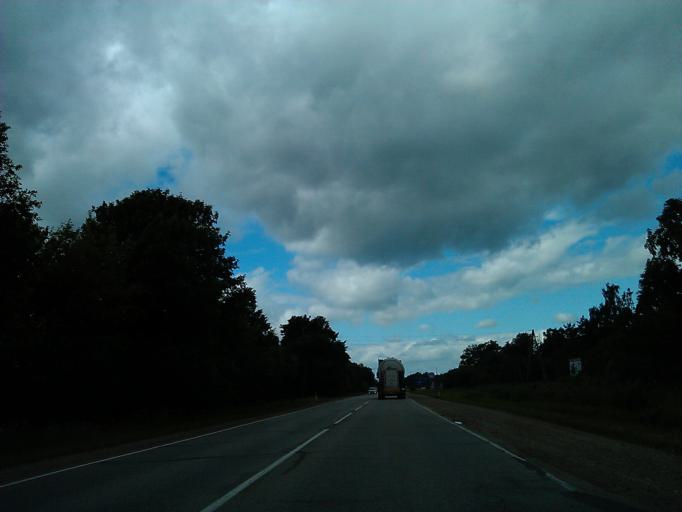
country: LV
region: Tukuma Rajons
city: Tukums
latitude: 56.9312
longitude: 23.2086
